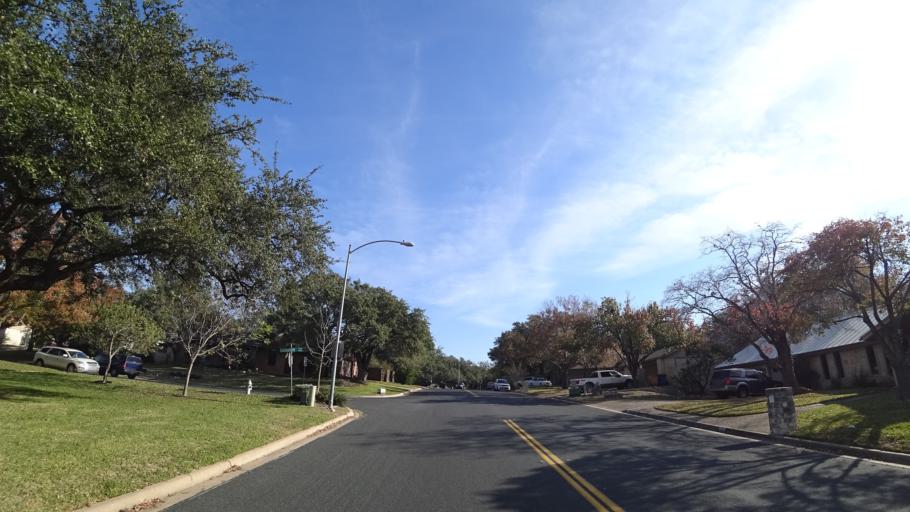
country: US
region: Texas
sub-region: Williamson County
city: Jollyville
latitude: 30.3821
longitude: -97.7613
